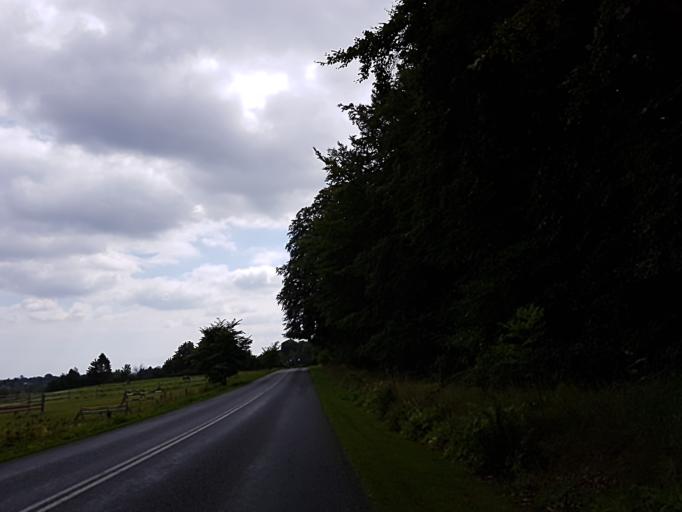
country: DK
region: Capital Region
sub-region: Fureso Kommune
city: Farum
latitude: 55.8120
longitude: 12.3194
